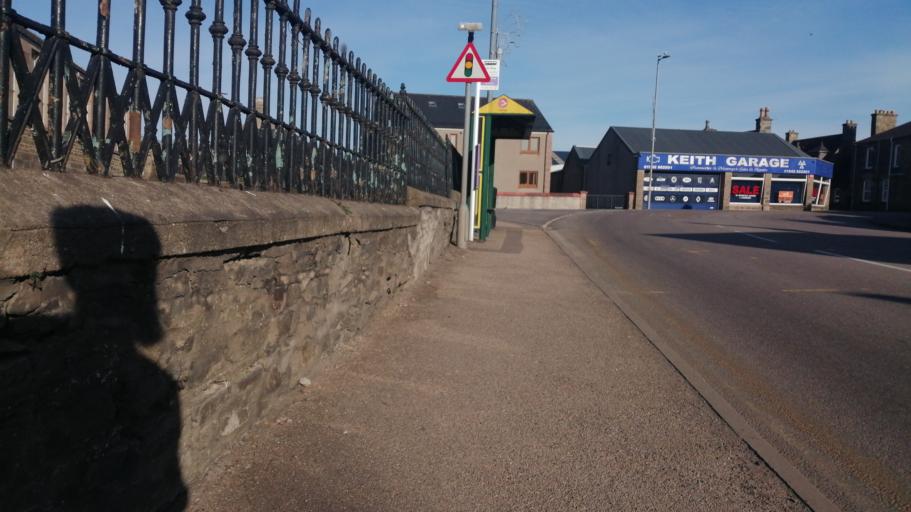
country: GB
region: Scotland
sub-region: Moray
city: Keith
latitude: 57.5429
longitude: -2.9485
